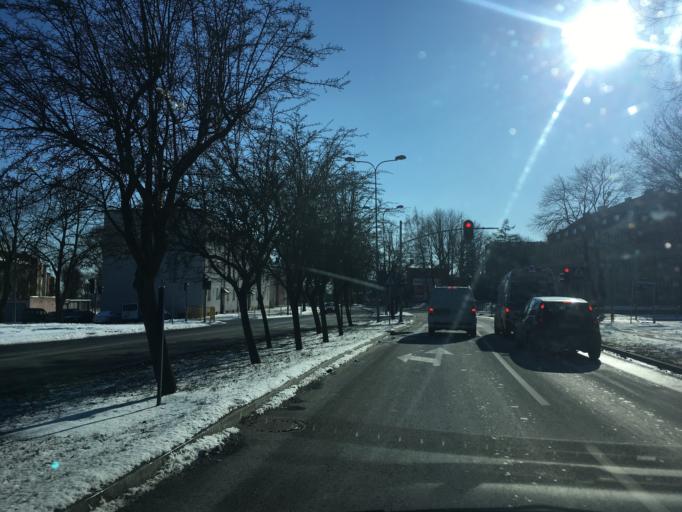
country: PL
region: Pomeranian Voivodeship
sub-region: Slupsk
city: Slupsk
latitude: 54.4661
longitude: 17.0116
